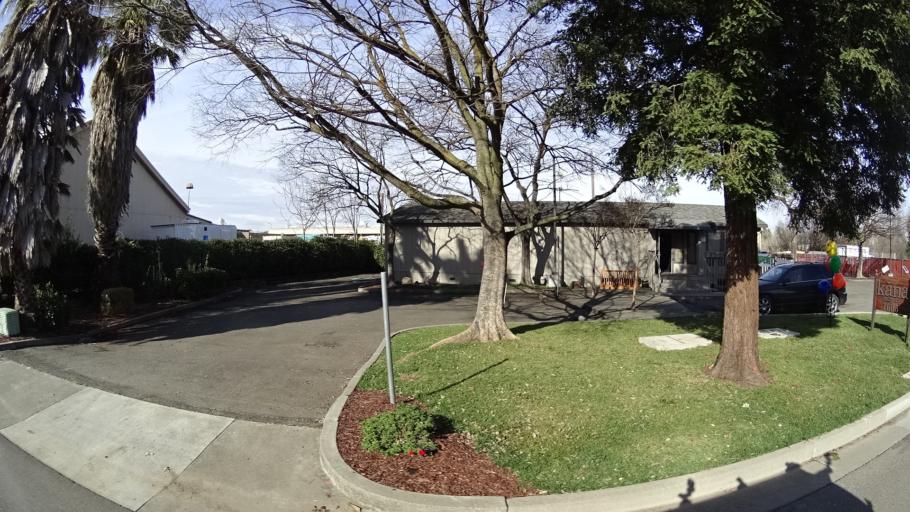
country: US
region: California
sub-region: Yolo County
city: Davis
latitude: 38.5453
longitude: -121.7311
